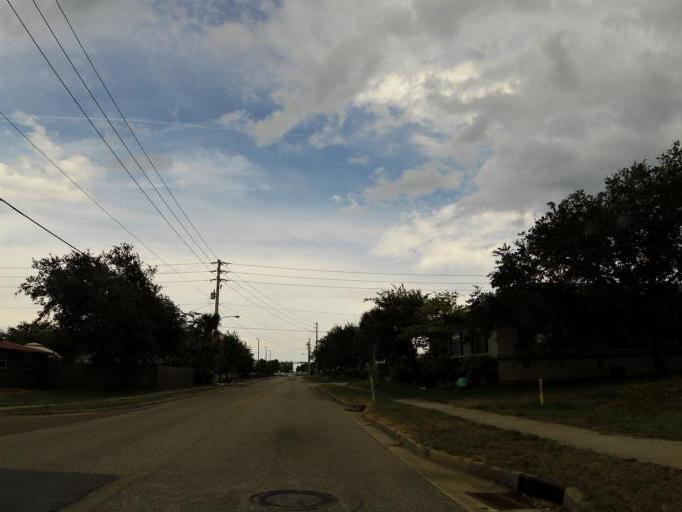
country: US
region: Florida
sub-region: Duval County
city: Jacksonville Beach
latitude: 30.2675
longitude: -81.3912
